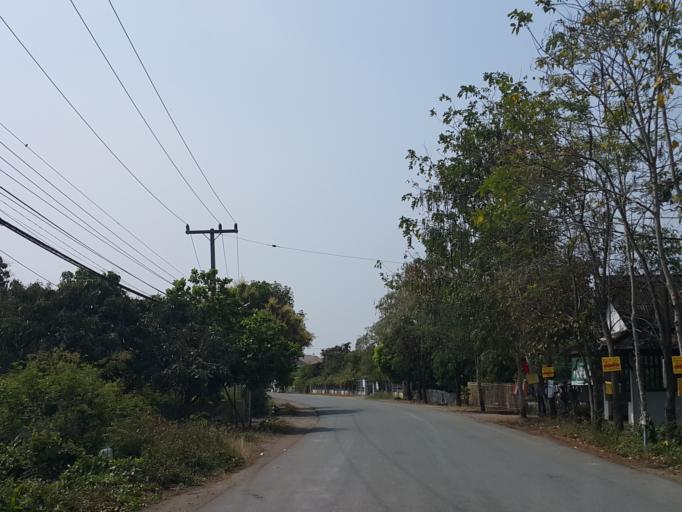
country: TH
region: Lamphun
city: Ban Thi
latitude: 18.6763
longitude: 99.1002
